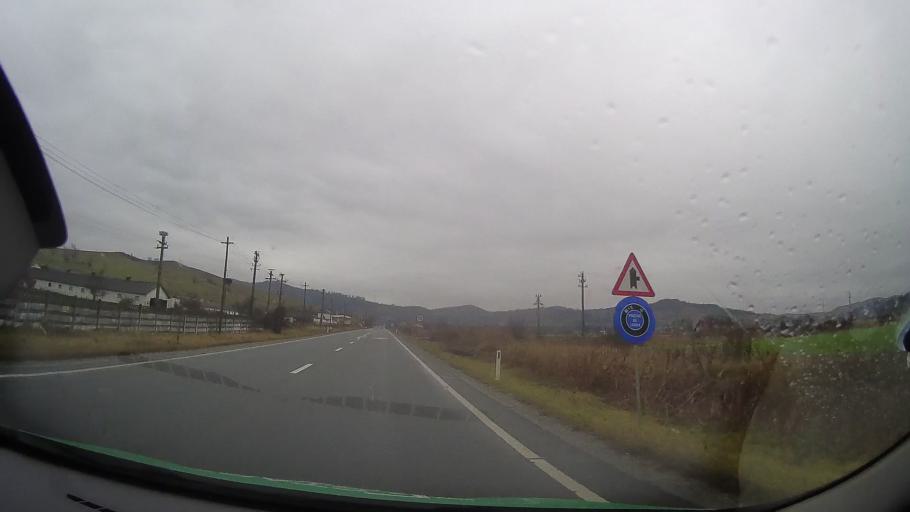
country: RO
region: Bistrita-Nasaud
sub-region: Comuna Teaca
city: Teaca
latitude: 46.9202
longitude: 24.4916
